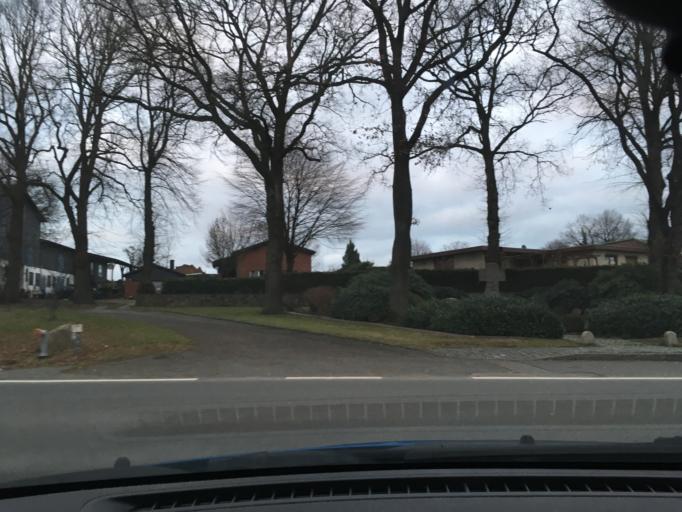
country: DE
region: Schleswig-Holstein
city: Kaaks
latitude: 53.9911
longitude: 9.4644
